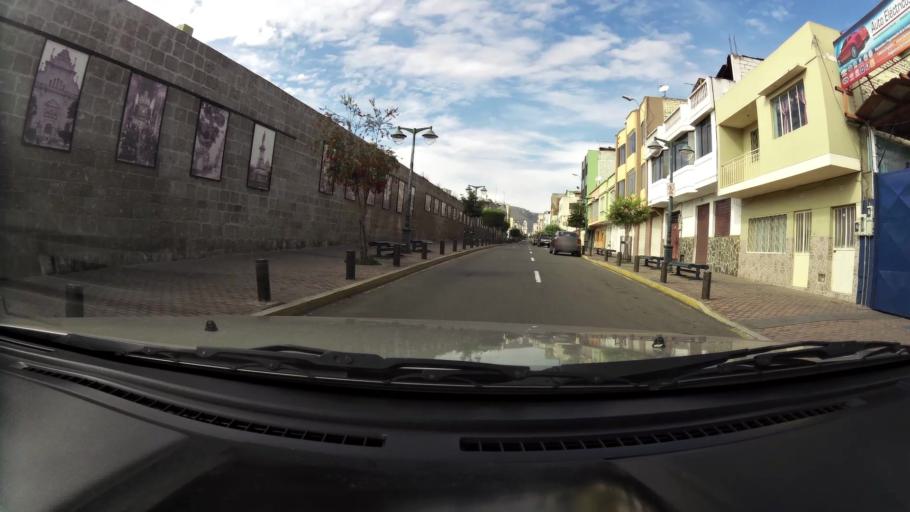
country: EC
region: Tungurahua
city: Ambato
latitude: -1.2337
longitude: -78.6213
